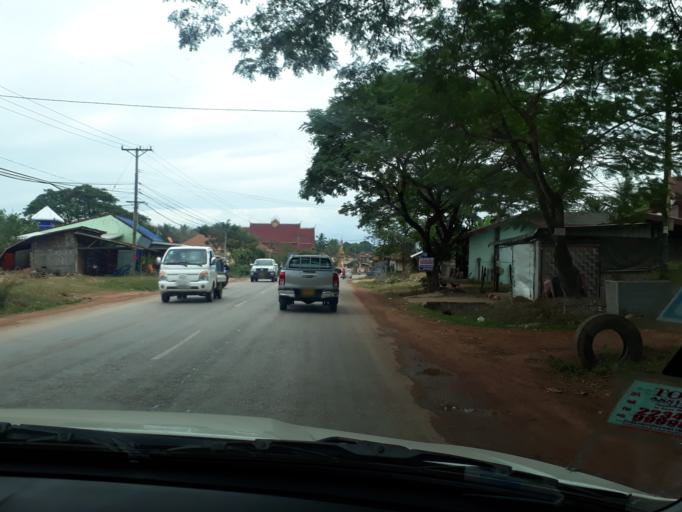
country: LA
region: Vientiane
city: Muang Phon-Hong
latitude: 18.3423
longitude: 102.4309
